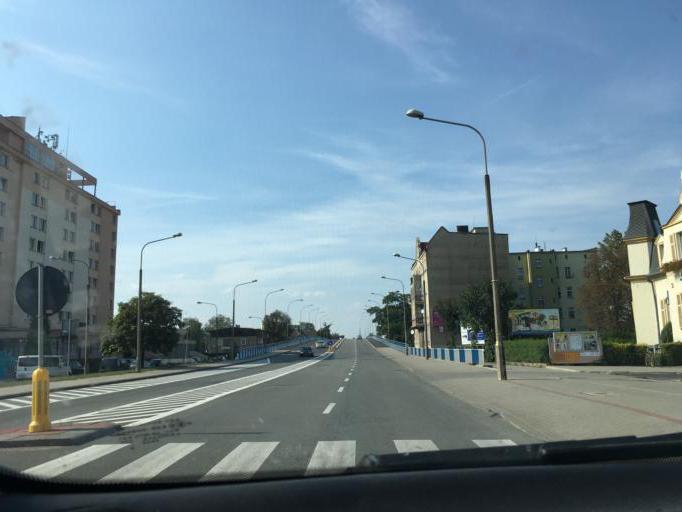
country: PL
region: Opole Voivodeship
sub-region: Powiat nyski
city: Nysa
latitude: 50.4603
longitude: 17.3491
